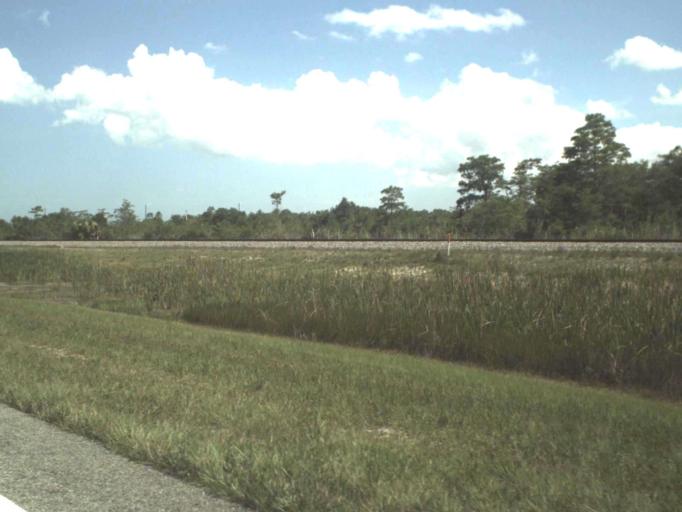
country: US
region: Florida
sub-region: Palm Beach County
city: Palm Beach Gardens
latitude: 26.8138
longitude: -80.1584
